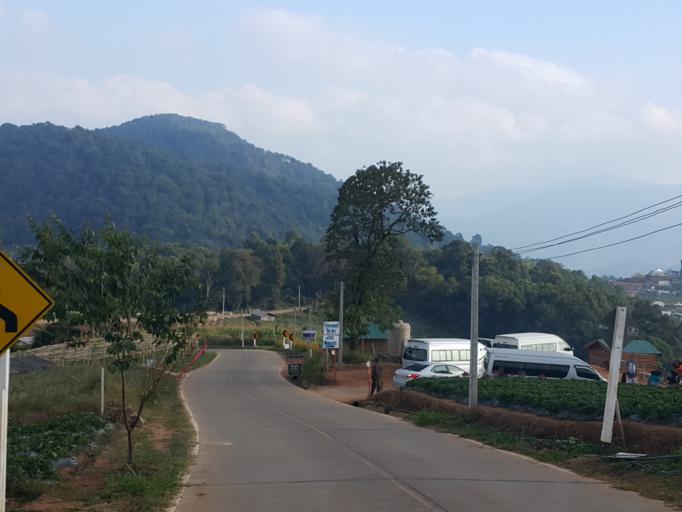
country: TH
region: Chiang Mai
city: Samoeng
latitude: 18.9306
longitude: 98.8173
